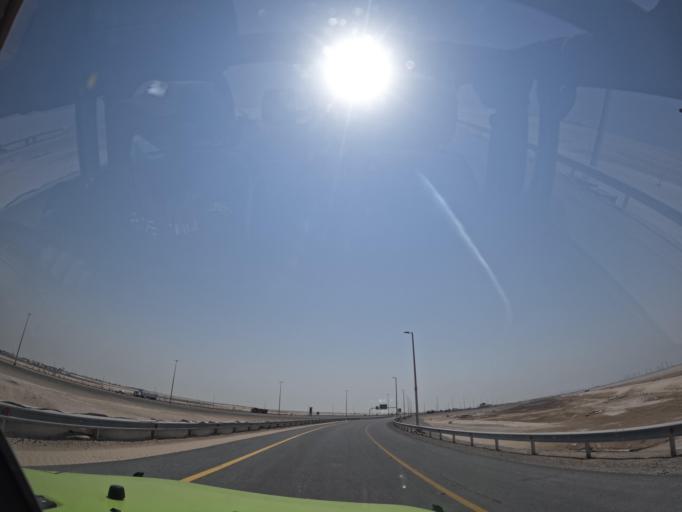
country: AE
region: Abu Dhabi
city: Abu Dhabi
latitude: 24.2448
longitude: 54.4691
